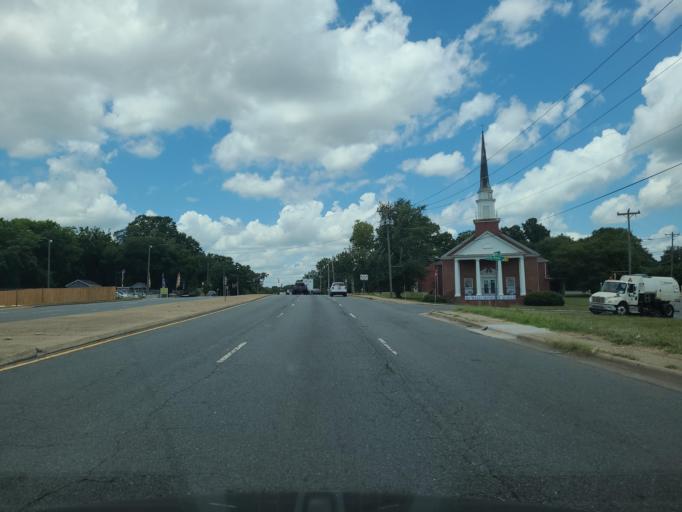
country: US
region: North Carolina
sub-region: Mecklenburg County
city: Charlotte
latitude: 35.2492
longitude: -80.8975
